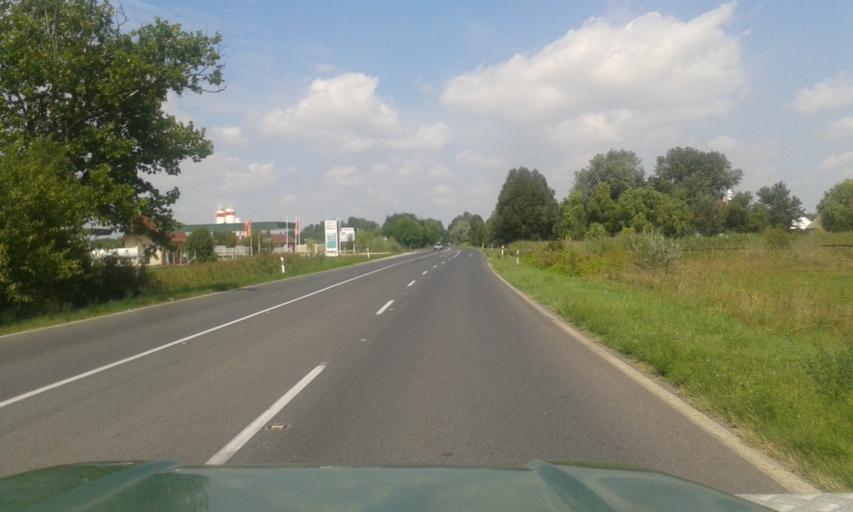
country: HU
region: Csongrad
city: Szatymaz
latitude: 46.3238
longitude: 20.0627
